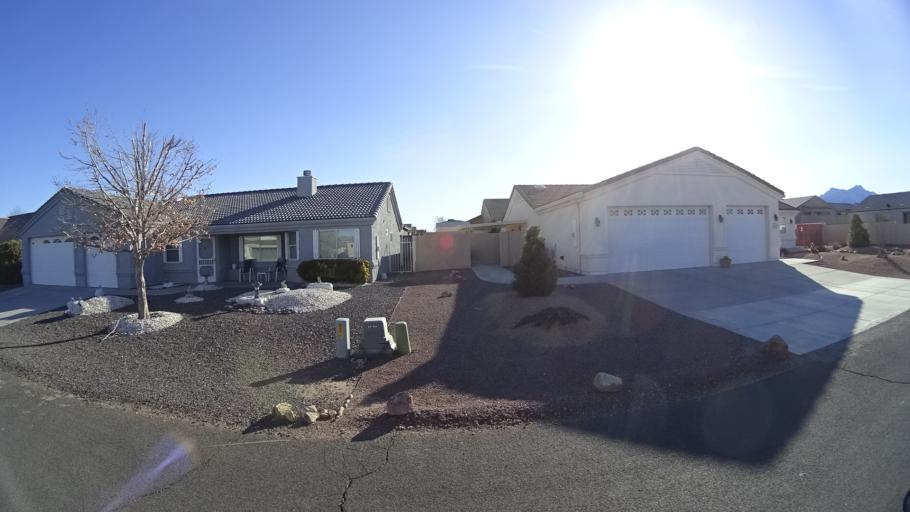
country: US
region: Arizona
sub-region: Mohave County
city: Kingman
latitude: 35.2124
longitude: -114.0060
